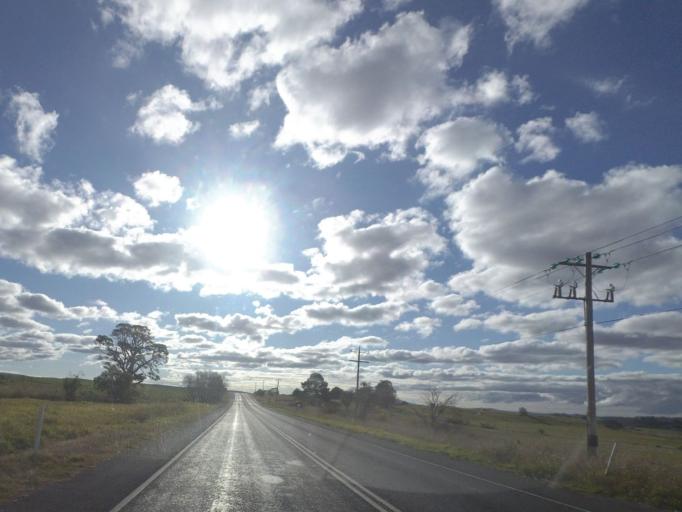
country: AU
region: Victoria
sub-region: Mount Alexander
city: Castlemaine
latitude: -37.1814
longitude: 144.3625
